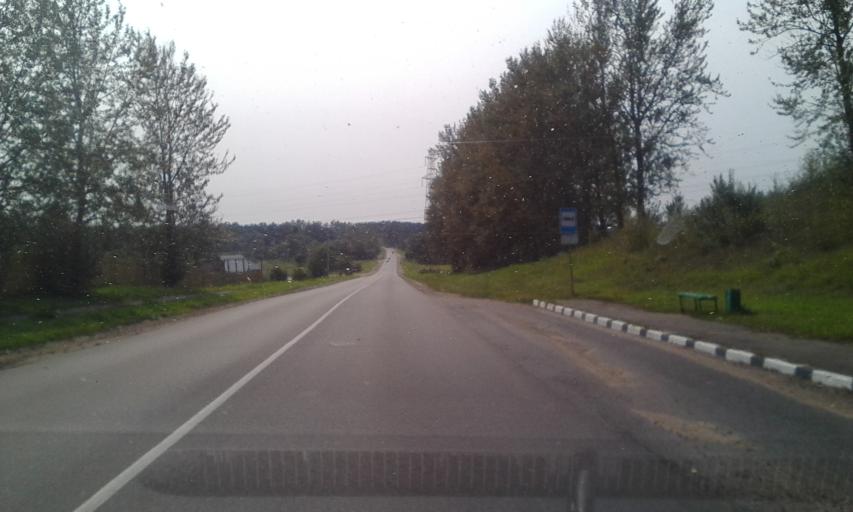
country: BY
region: Minsk
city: Hatava
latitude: 53.8072
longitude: 27.6464
